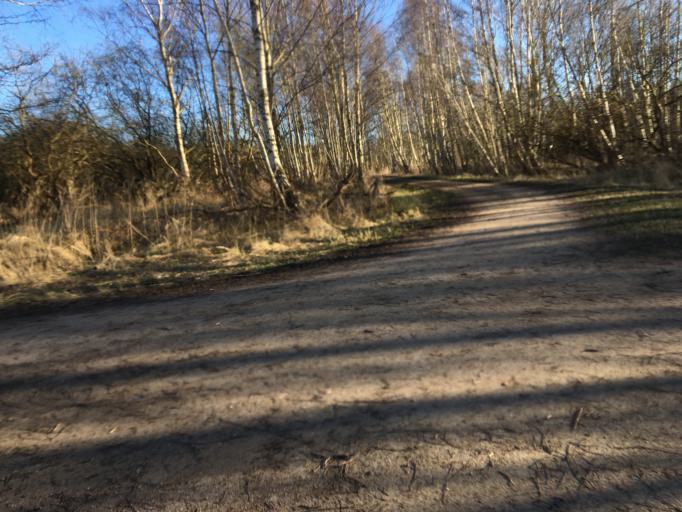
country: DK
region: Capital Region
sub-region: Tarnby Kommune
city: Tarnby
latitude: 55.5879
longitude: 12.5593
